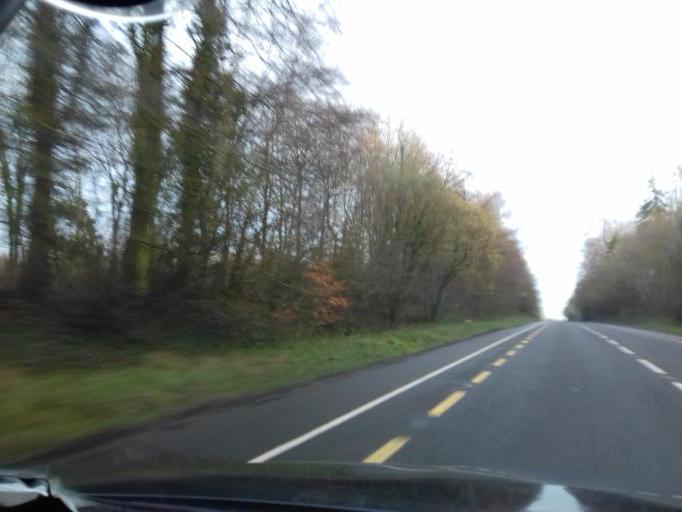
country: IE
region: Leinster
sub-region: Laois
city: Abbeyleix
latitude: 52.8678
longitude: -7.3660
